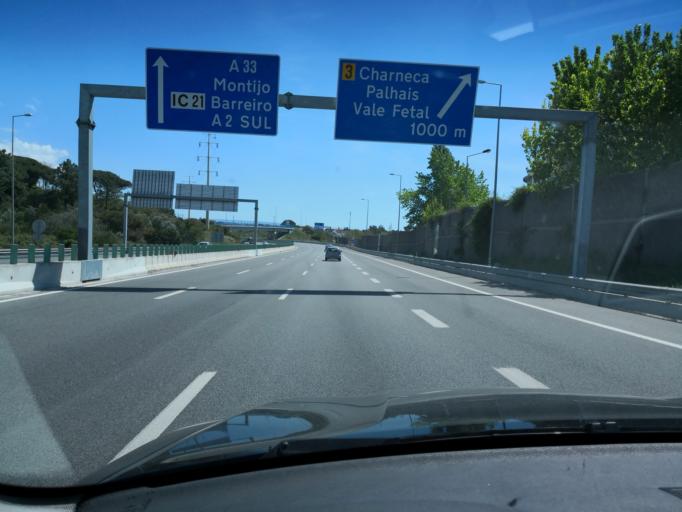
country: PT
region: Setubal
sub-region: Almada
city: Sobreda
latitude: 38.6433
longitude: -9.2018
